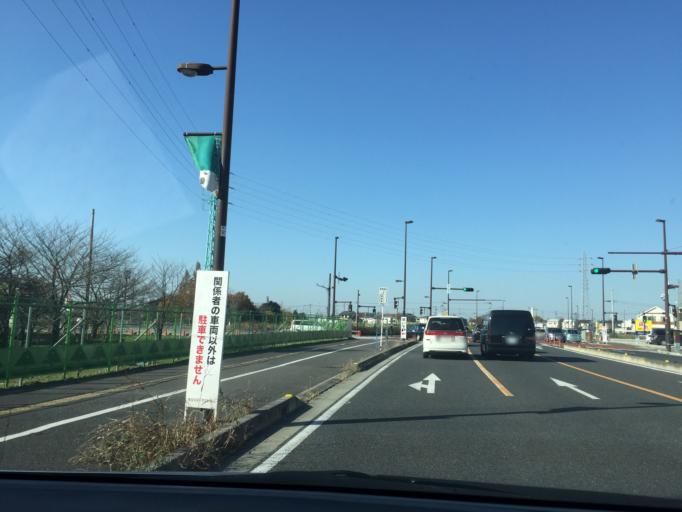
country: JP
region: Saitama
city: Iwatsuki
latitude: 35.9043
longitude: 139.7212
